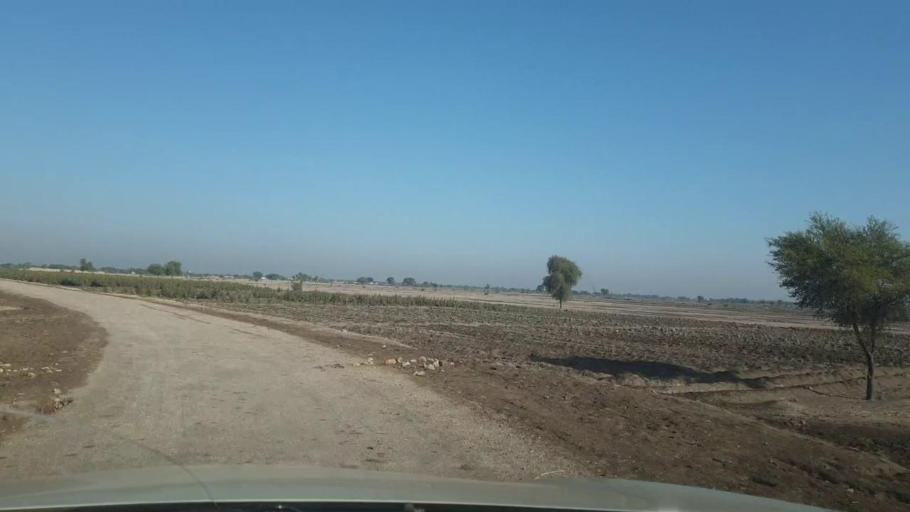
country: PK
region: Sindh
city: Bhan
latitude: 26.5207
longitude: 67.6744
